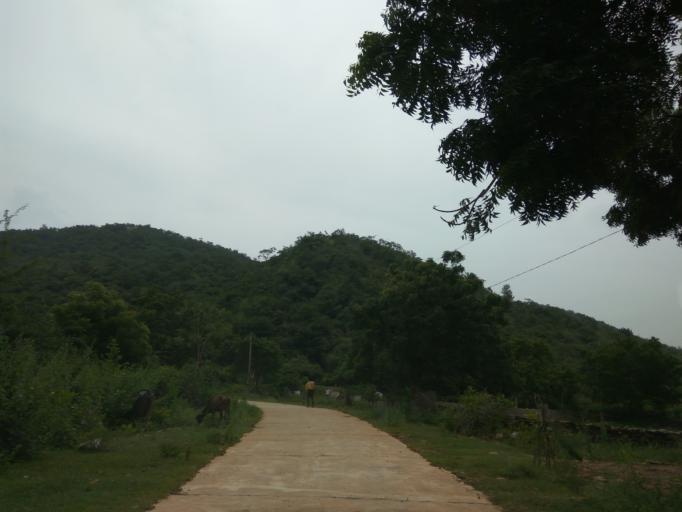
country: IN
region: Andhra Pradesh
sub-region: Prakasam
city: Cumbum
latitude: 15.4434
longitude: 79.0821
